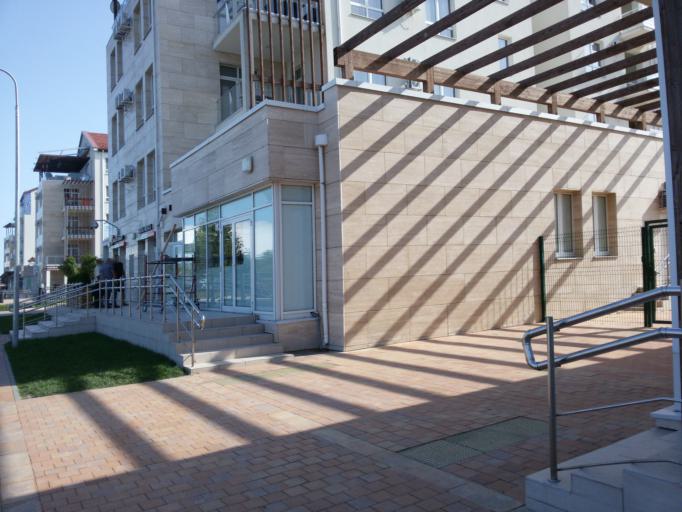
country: RU
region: Krasnodarskiy
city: Adler
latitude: 43.4060
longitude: 39.9445
